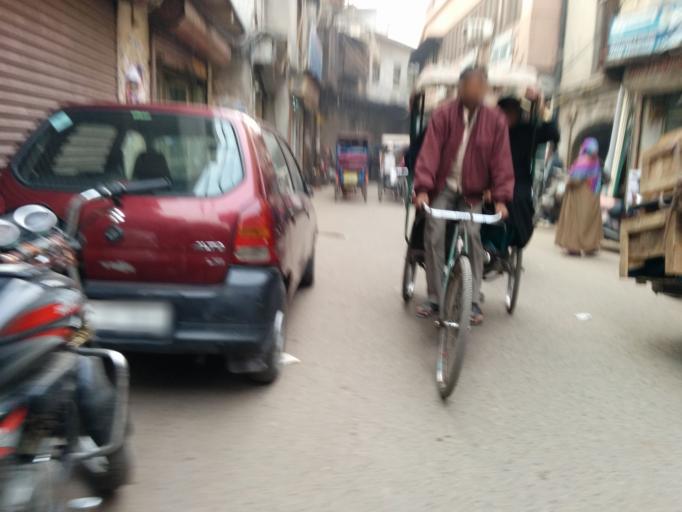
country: IN
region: NCT
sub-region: North Delhi
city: Delhi
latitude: 28.6495
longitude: 77.2292
